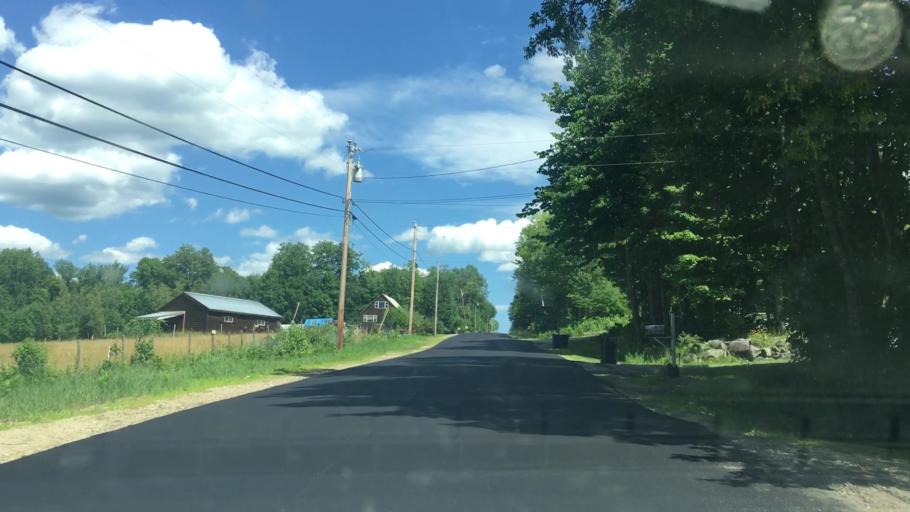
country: US
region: Maine
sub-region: Franklin County
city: Wilton
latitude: 44.5751
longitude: -70.1625
